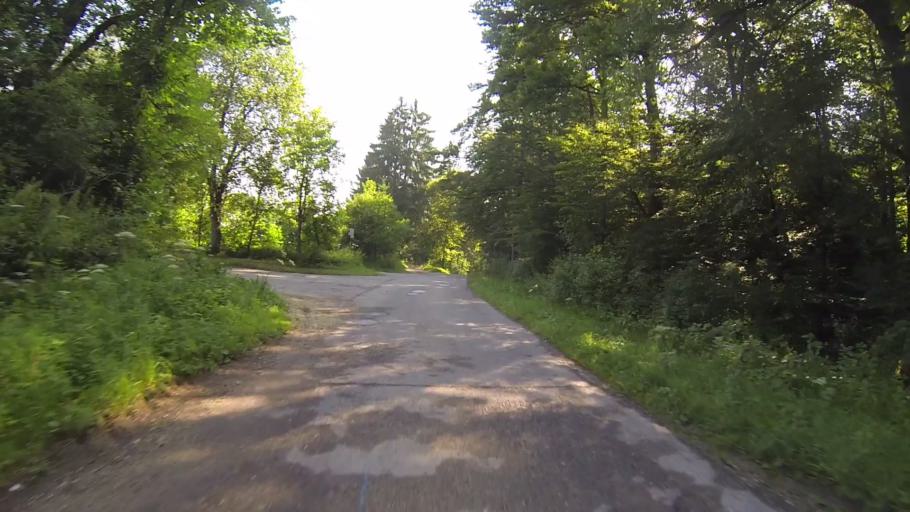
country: DE
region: Baden-Wuerttemberg
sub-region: Regierungsbezirk Stuttgart
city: Konigsbronn
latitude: 48.7263
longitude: 10.1141
